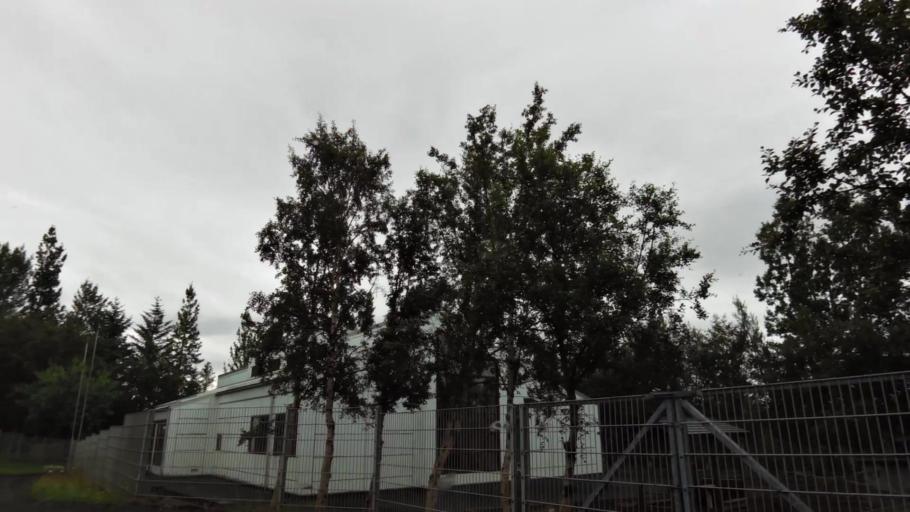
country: IS
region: Capital Region
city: Reykjavik
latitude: 64.1350
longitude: -21.8112
